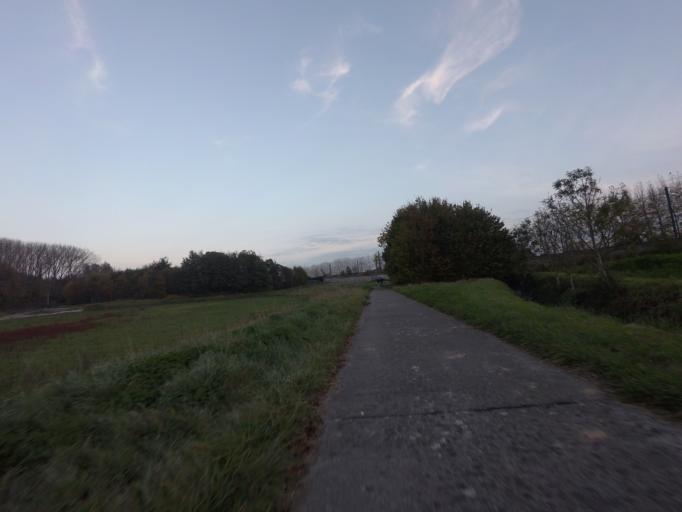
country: BE
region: Flanders
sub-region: Provincie Vlaams-Brabant
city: Zaventem
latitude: 50.8830
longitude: 4.4980
